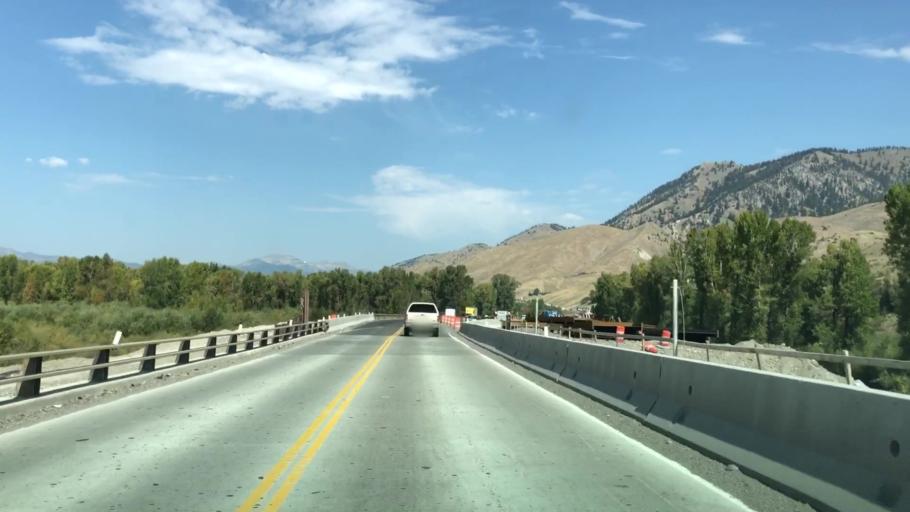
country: US
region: Wyoming
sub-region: Teton County
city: South Park
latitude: 43.3849
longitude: -110.7456
